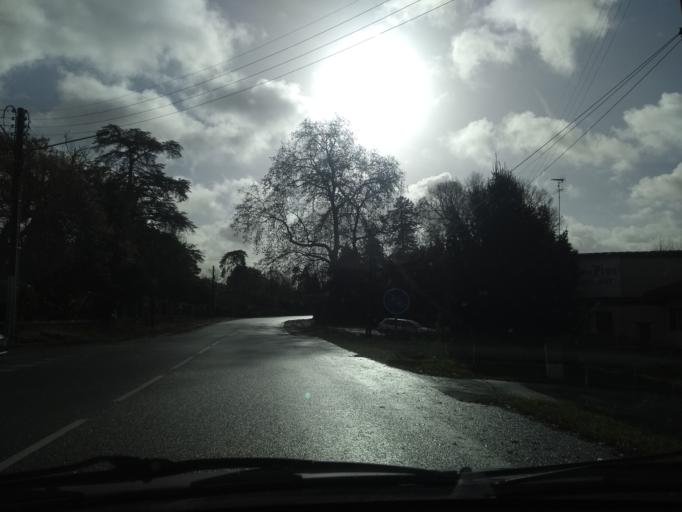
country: FR
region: Aquitaine
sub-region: Departement de la Gironde
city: Belin-Beliet
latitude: 44.4971
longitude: -0.7902
